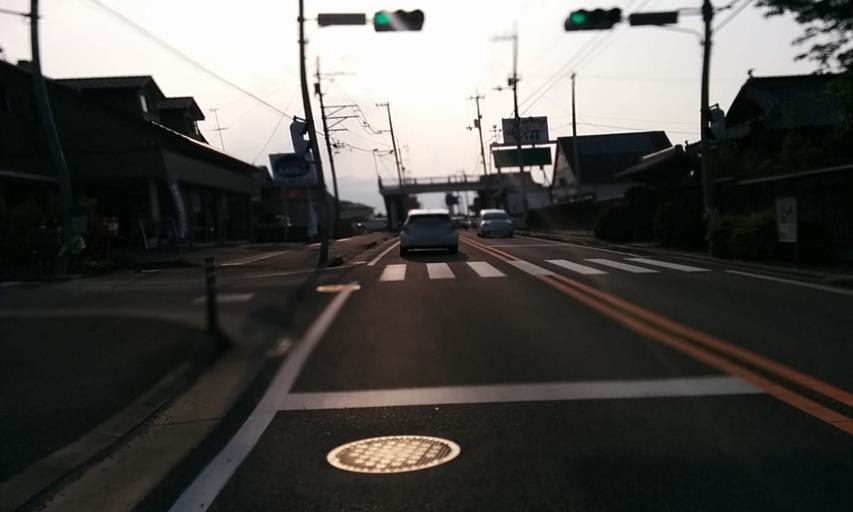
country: JP
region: Ehime
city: Saijo
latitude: 33.8955
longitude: 133.1281
